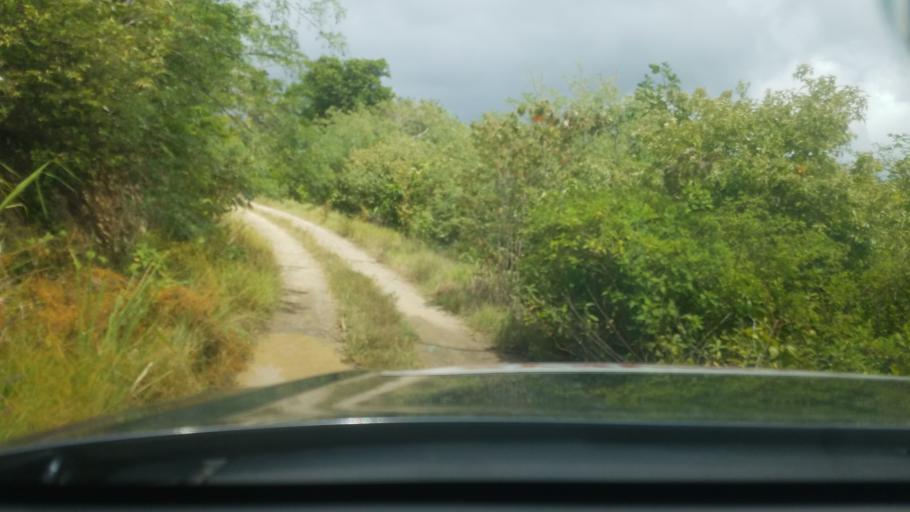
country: LC
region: Praslin
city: Praslin
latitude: 13.8688
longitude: -60.8946
